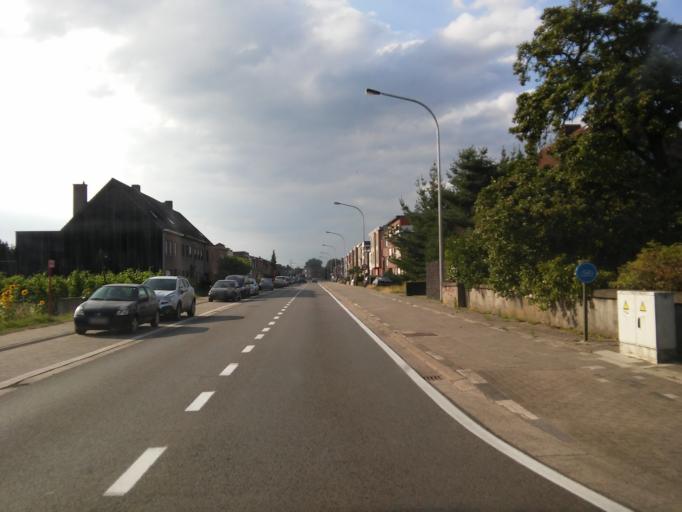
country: BE
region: Flanders
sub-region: Provincie Antwerpen
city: Duffel
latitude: 51.0999
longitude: 4.5058
